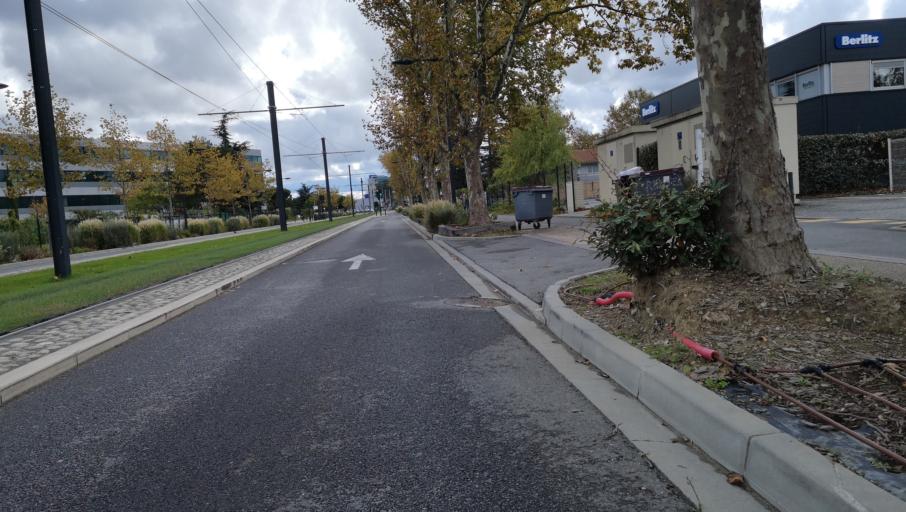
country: FR
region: Midi-Pyrenees
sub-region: Departement de la Haute-Garonne
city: Blagnac
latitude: 43.6280
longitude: 1.3805
